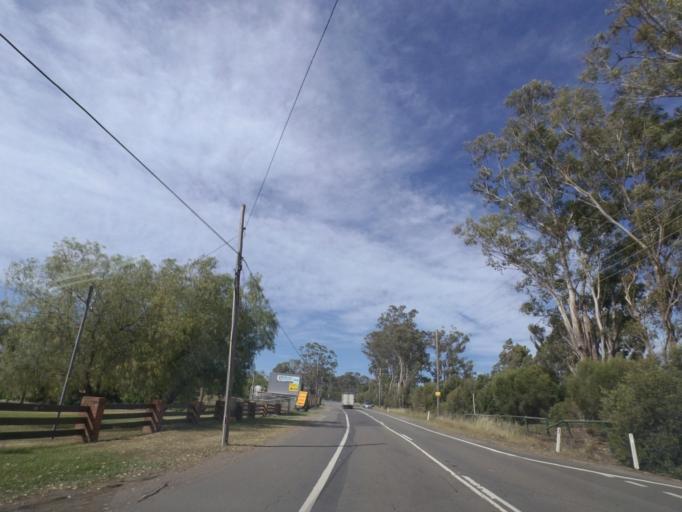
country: AU
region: New South Wales
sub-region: Campbelltown Municipality
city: Denham Court
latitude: -33.9821
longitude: 150.8474
